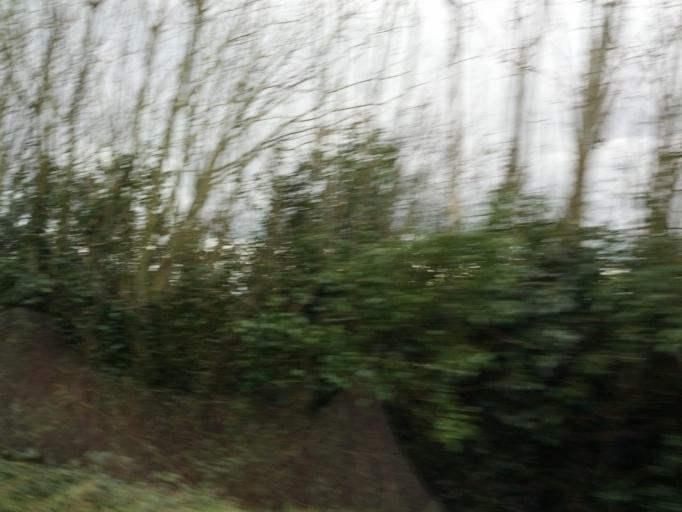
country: IE
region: Connaught
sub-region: County Galway
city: Athenry
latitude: 53.4657
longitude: -8.5744
